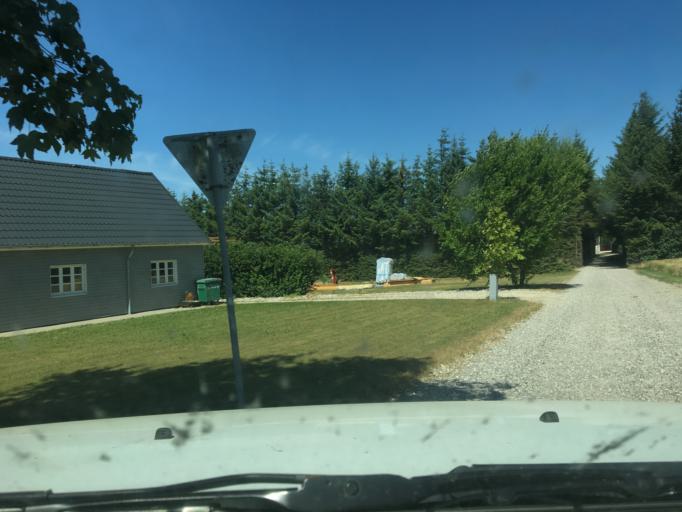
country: DK
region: Central Jutland
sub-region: Favrskov Kommune
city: Ulstrup
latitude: 56.4111
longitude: 9.7520
